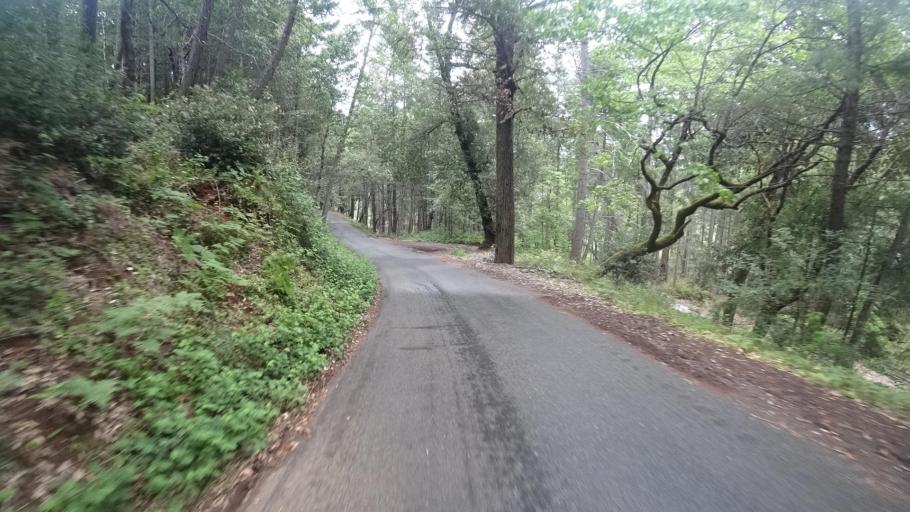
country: US
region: California
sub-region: Siskiyou County
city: Happy Camp
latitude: 41.3695
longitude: -123.5028
